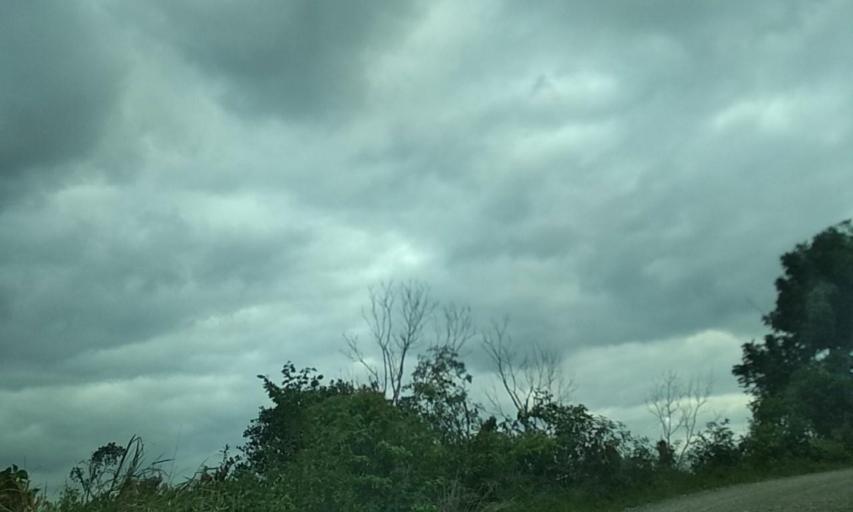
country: MX
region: Veracruz
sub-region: Papantla
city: Polutla
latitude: 20.5180
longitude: -97.2960
